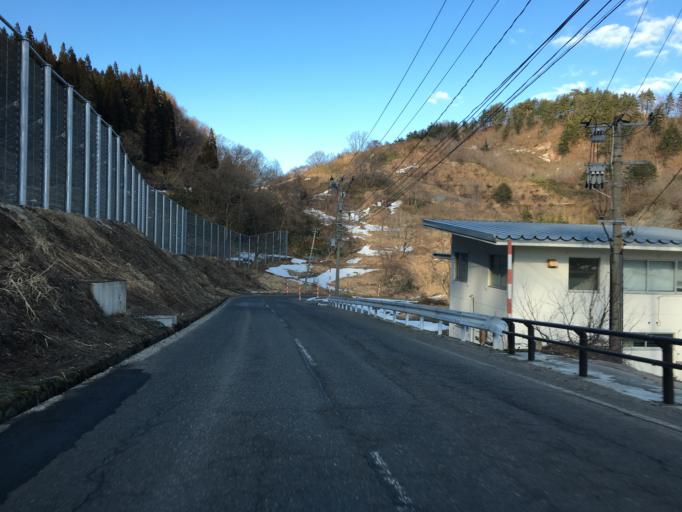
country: JP
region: Yamagata
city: Nagai
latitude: 37.9760
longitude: 139.9198
